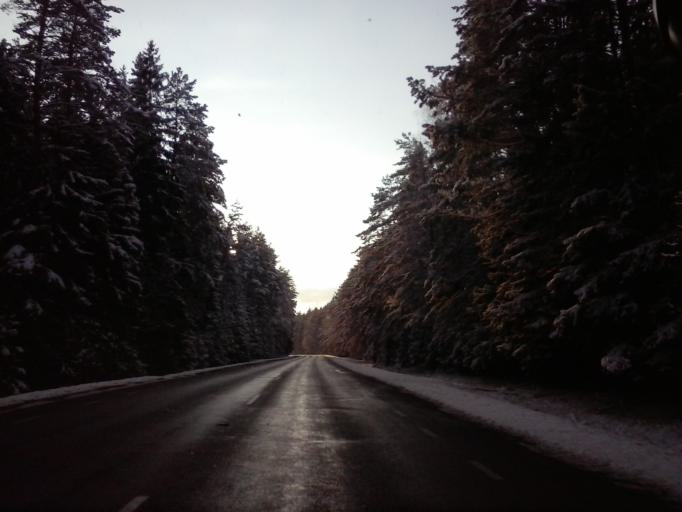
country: EE
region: Tartu
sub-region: UElenurme vald
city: Ulenurme
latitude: 58.3410
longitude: 26.9038
